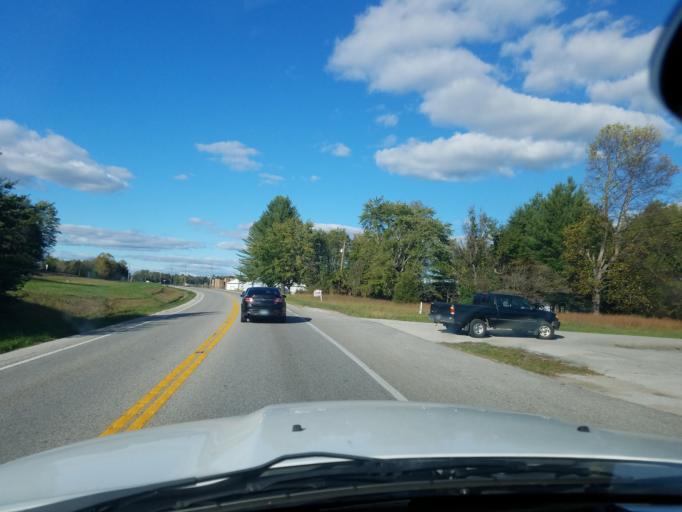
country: US
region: Kentucky
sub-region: Laurel County
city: London
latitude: 37.0471
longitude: -84.0525
